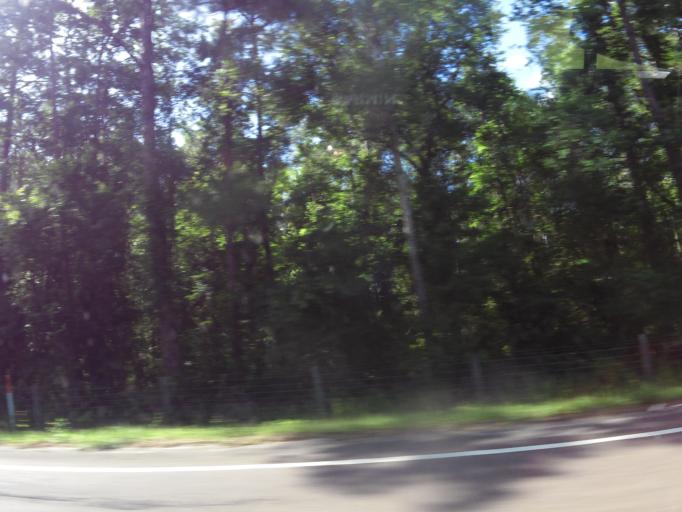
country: US
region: Florida
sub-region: Nassau County
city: Callahan
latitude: 30.5610
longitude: -81.8515
